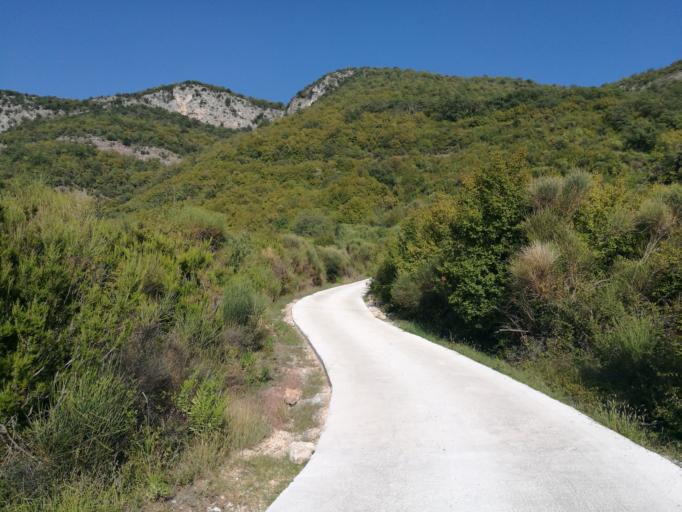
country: ME
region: Budva
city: Budva
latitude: 42.2850
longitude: 18.8881
